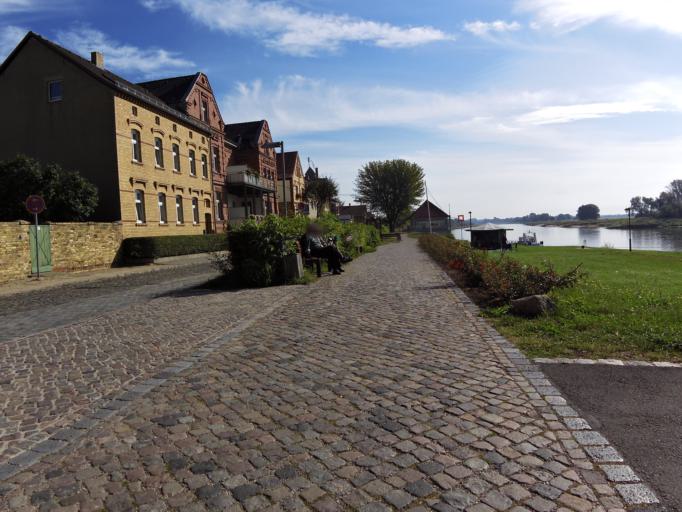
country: DE
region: Saxony-Anhalt
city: Wittenburg
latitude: 51.8634
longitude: 12.6099
